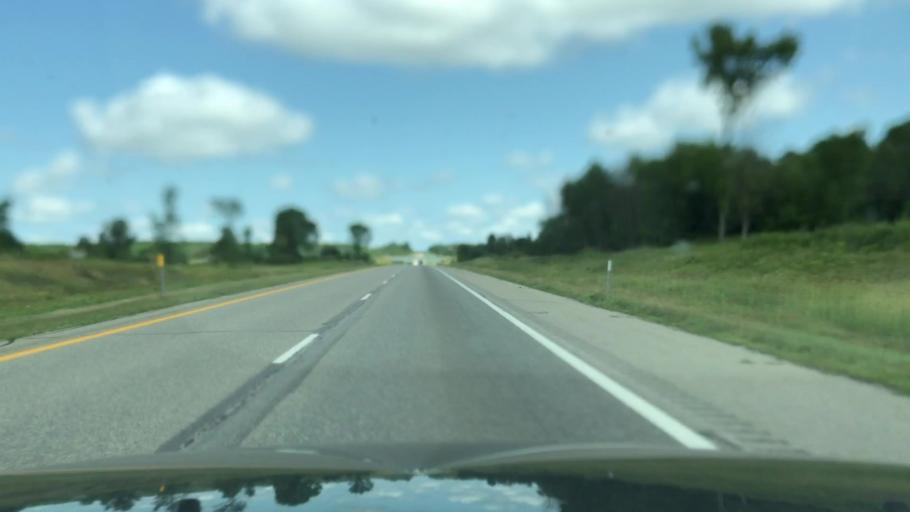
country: US
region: Michigan
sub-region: Mecosta County
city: Big Rapids
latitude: 43.7092
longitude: -85.5290
